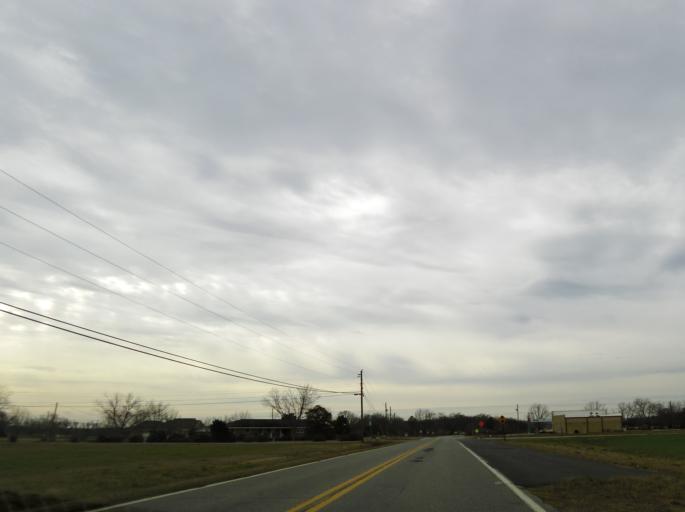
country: US
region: Georgia
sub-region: Peach County
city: Byron
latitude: 32.7190
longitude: -83.7231
